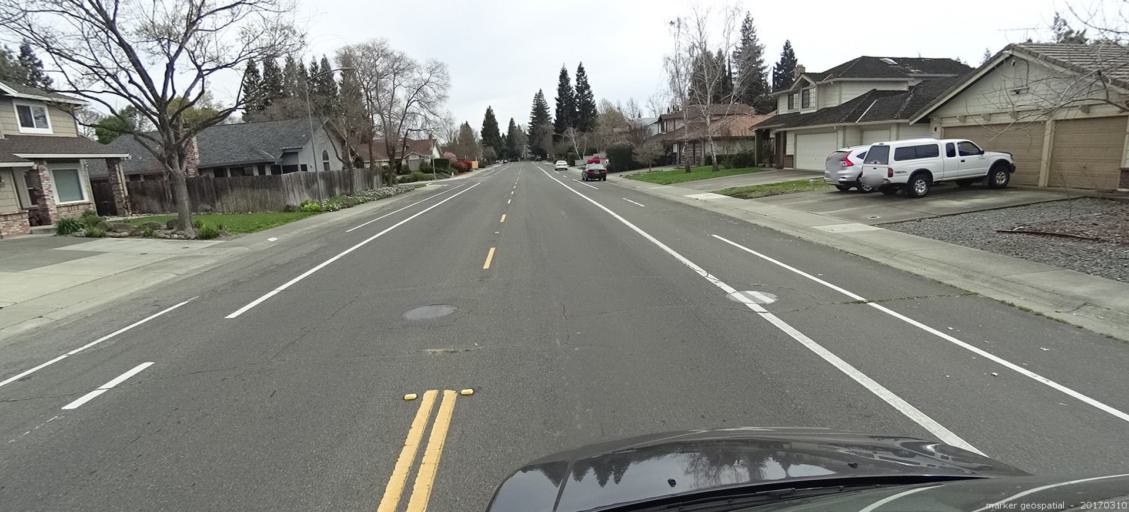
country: US
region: California
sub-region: Sacramento County
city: Parkway
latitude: 38.4879
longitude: -121.5224
